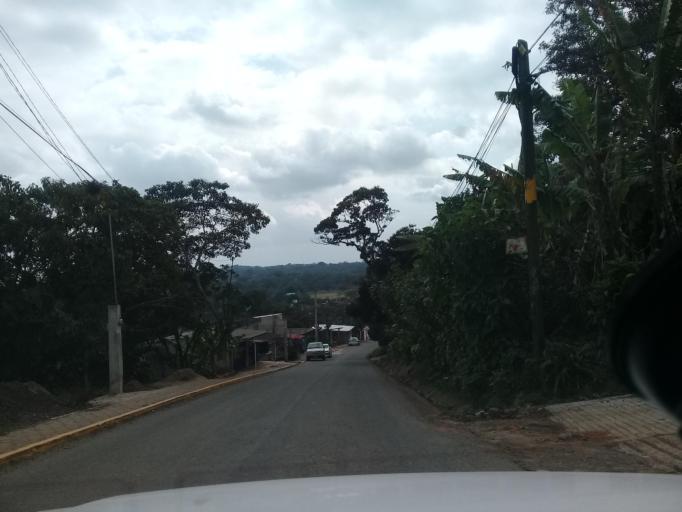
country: MX
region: Veracruz
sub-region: Xalapa
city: Fraccionamiento las Fuentes
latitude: 19.4777
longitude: -96.8776
